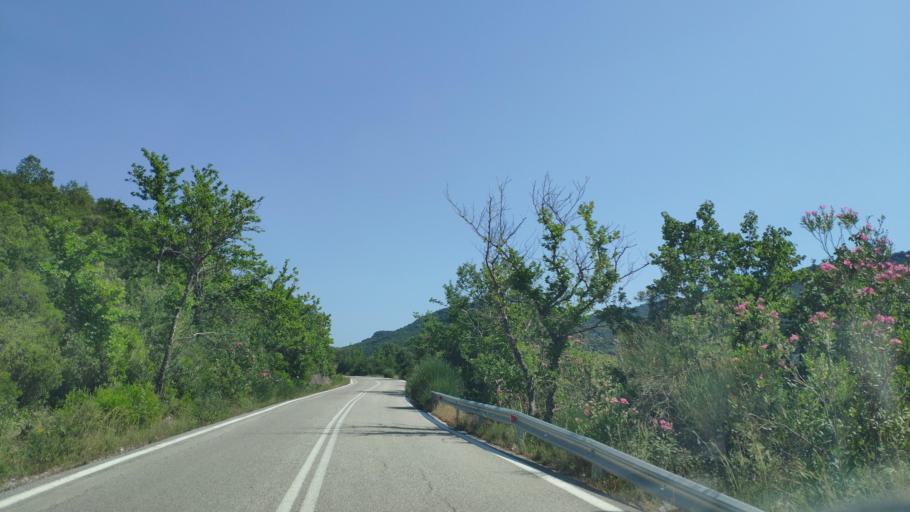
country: GR
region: West Greece
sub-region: Nomos Aitolias kai Akarnanias
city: Lepenou
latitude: 38.7731
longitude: 21.3357
